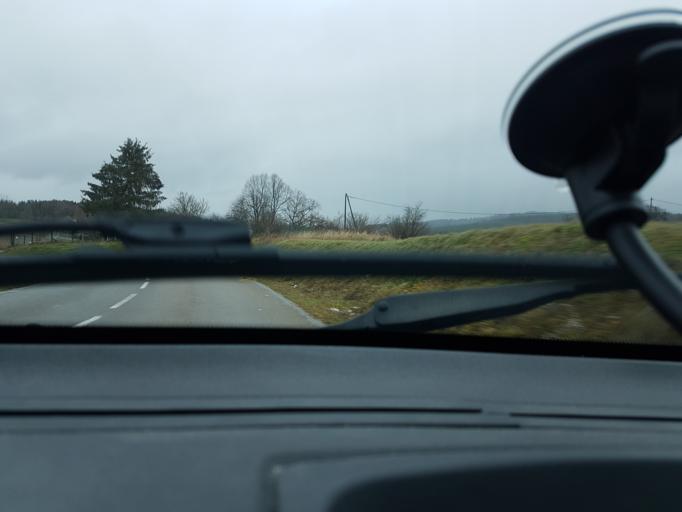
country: FR
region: Franche-Comte
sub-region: Departement du Doubs
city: Valdahon
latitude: 47.1406
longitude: 6.3733
